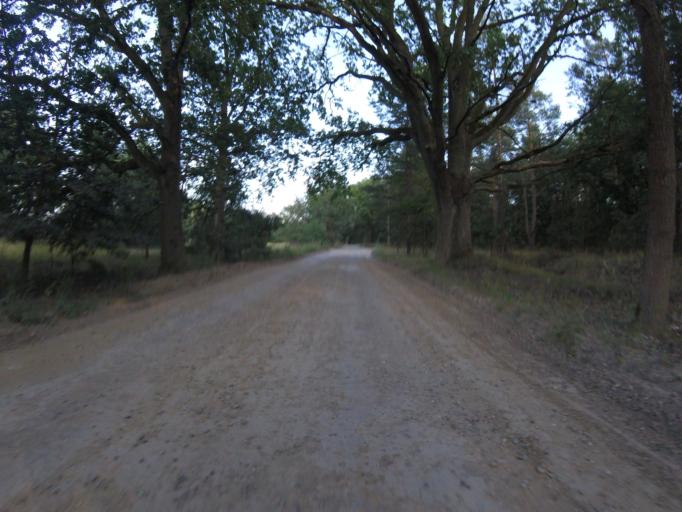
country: DE
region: Brandenburg
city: Zossen
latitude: 52.2084
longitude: 13.4852
